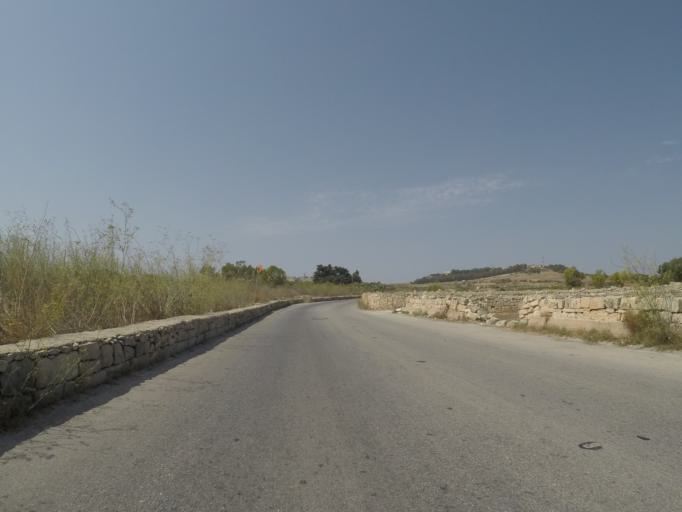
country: MT
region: L-Imtarfa
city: Imtarfa
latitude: 35.8988
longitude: 14.4133
